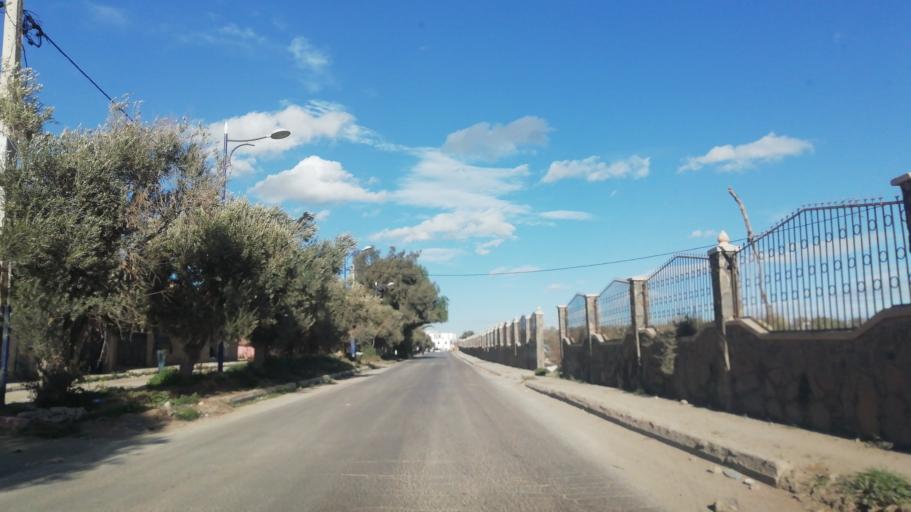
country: DZ
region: Oran
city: Sidi ech Chahmi
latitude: 35.6543
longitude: -0.5273
